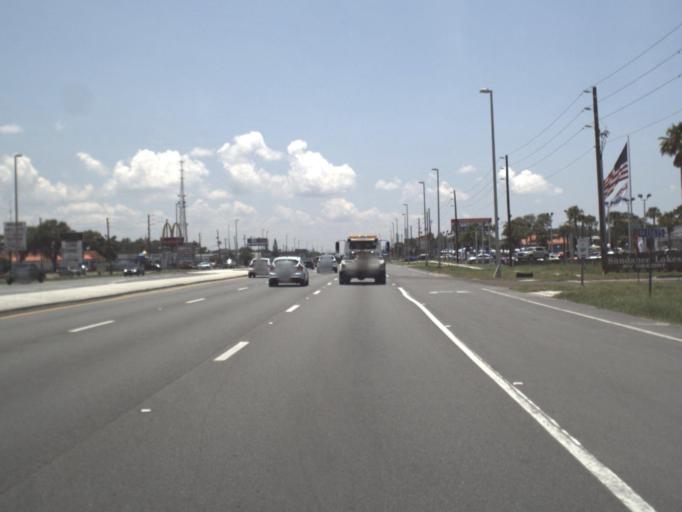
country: US
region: Florida
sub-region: Pasco County
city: Bayonet Point
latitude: 28.3278
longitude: -82.6994
